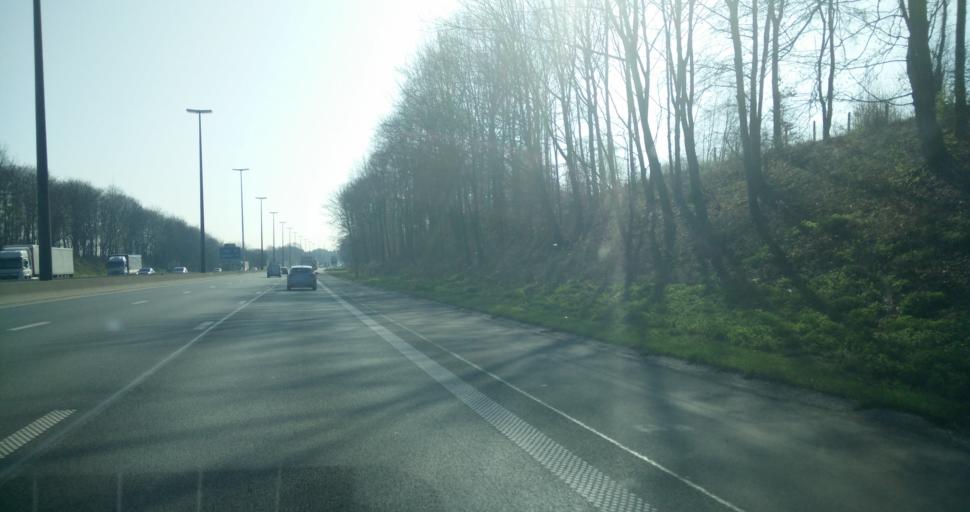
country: BE
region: Wallonia
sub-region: Province du Hainaut
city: Brunehault
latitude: 50.4806
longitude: 4.4592
